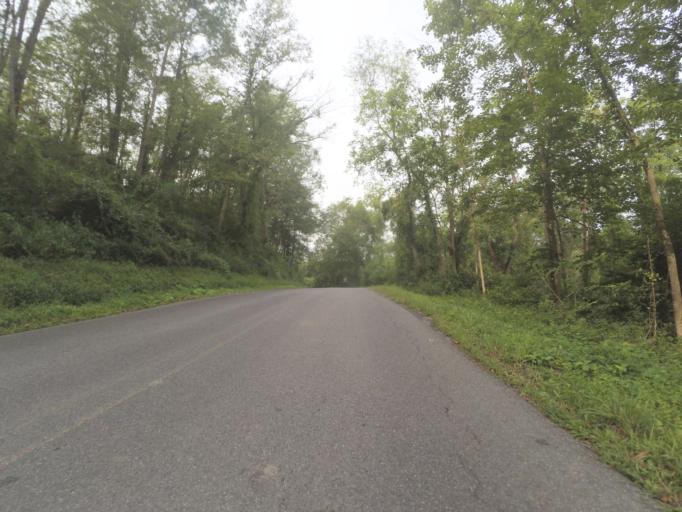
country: US
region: Pennsylvania
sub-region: Huntingdon County
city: McConnellstown
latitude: 40.5502
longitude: -78.1015
